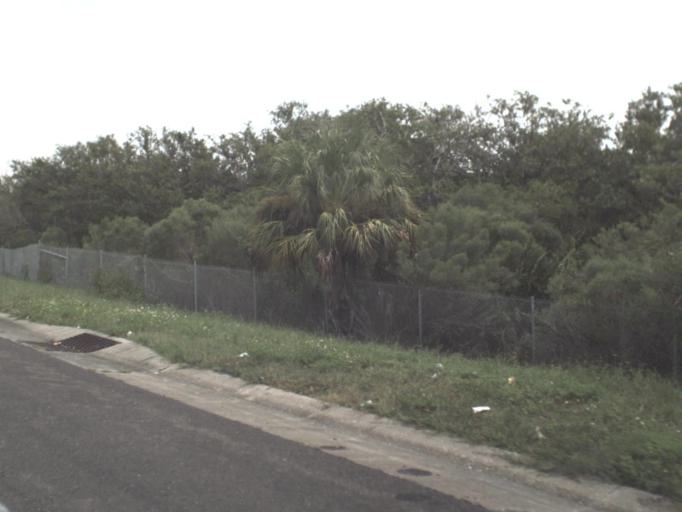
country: US
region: Florida
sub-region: Manatee County
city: Ellenton
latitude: 27.4981
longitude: -82.5191
